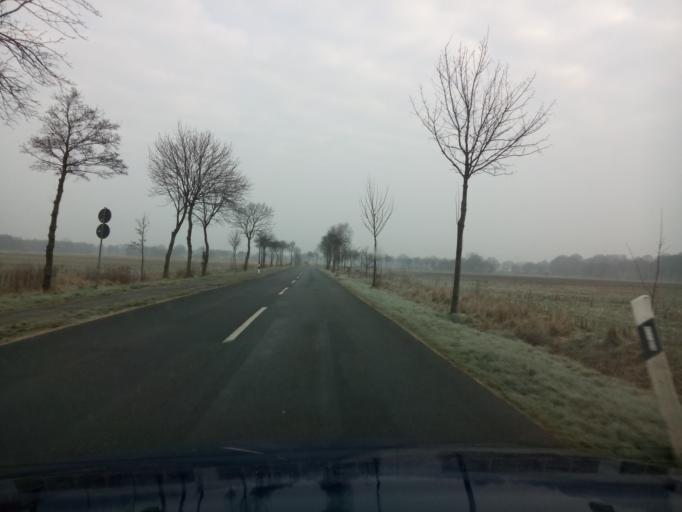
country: DE
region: Lower Saxony
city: Langen
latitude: 53.5835
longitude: 8.6386
